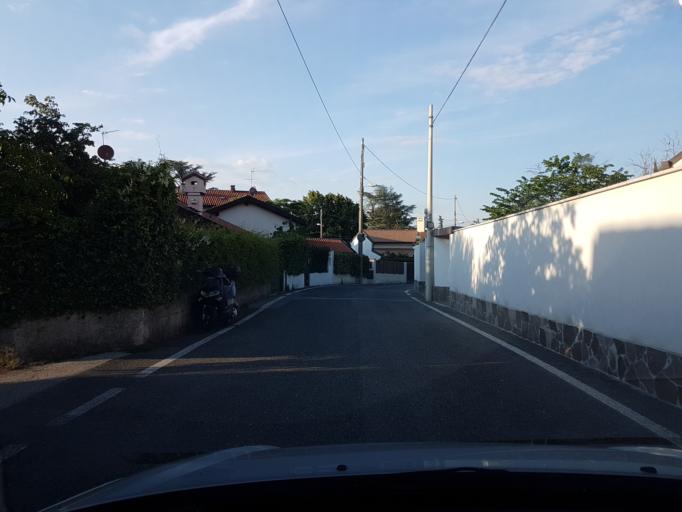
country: IT
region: Friuli Venezia Giulia
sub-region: Provincia di Trieste
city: Villa Opicina
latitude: 45.6877
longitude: 13.7817
